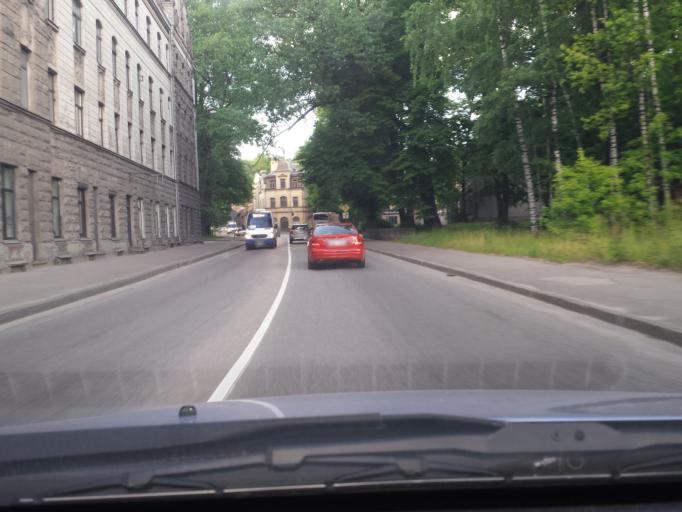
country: LV
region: Riga
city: Riga
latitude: 56.9581
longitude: 24.0704
